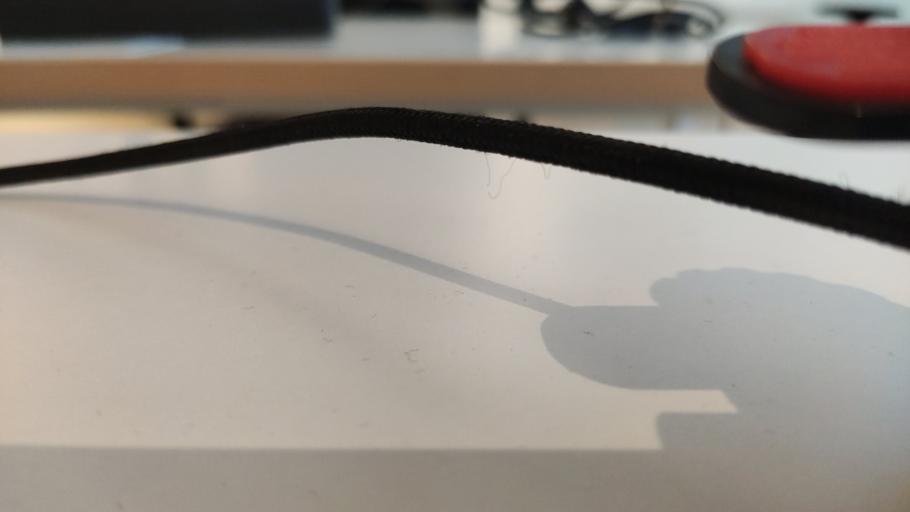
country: RU
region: Moskovskaya
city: Novopetrovskoye
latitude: 55.9137
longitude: 36.4408
